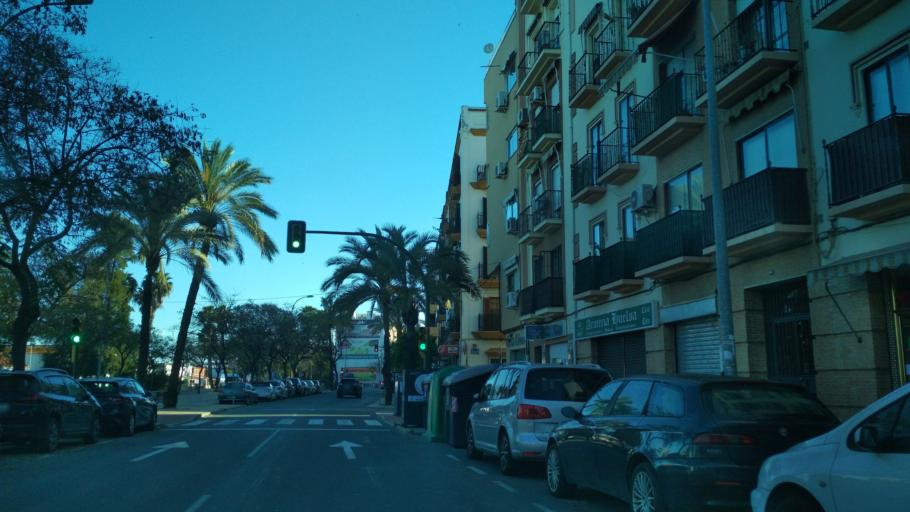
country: ES
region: Andalusia
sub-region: Provincia de Huelva
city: Huelva
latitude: 37.2675
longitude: -6.9519
